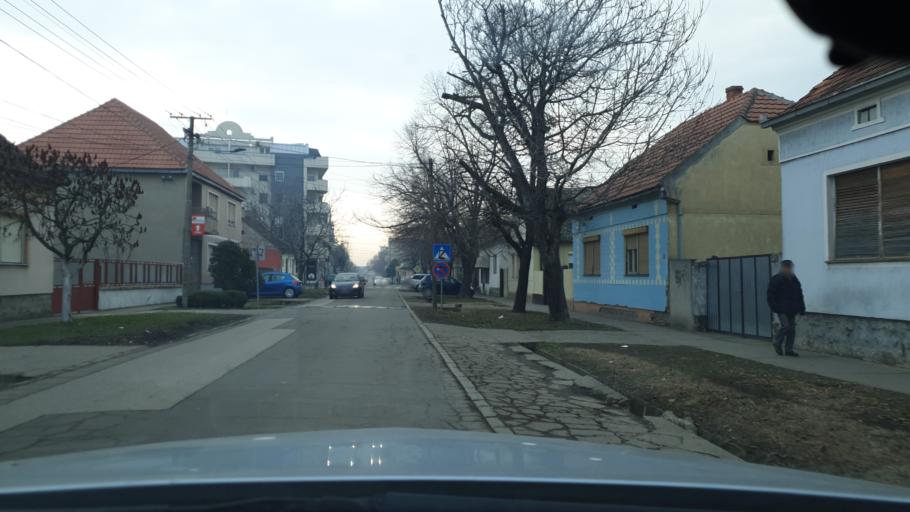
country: RS
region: Autonomna Pokrajina Vojvodina
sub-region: Sremski Okrug
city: Stara Pazova
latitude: 44.9874
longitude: 20.1629
